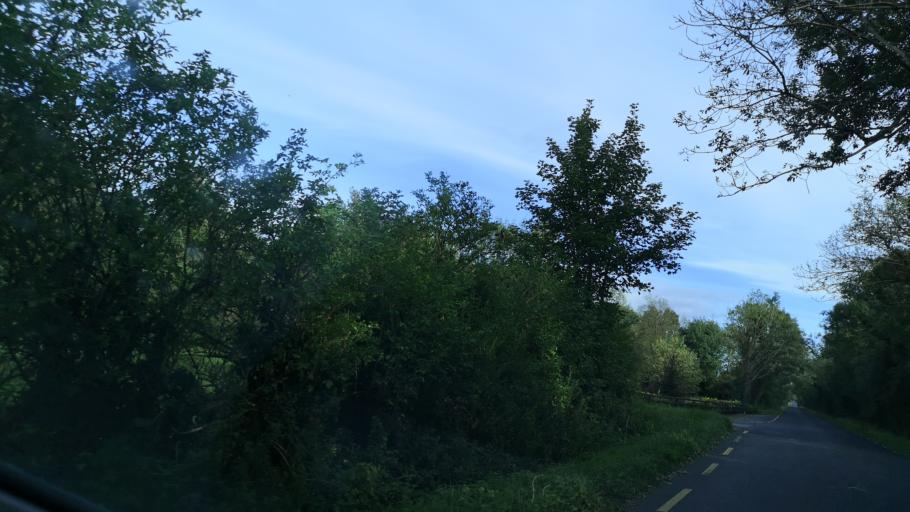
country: IE
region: Connaught
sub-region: County Galway
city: Ballinasloe
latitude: 53.3375
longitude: -8.2885
